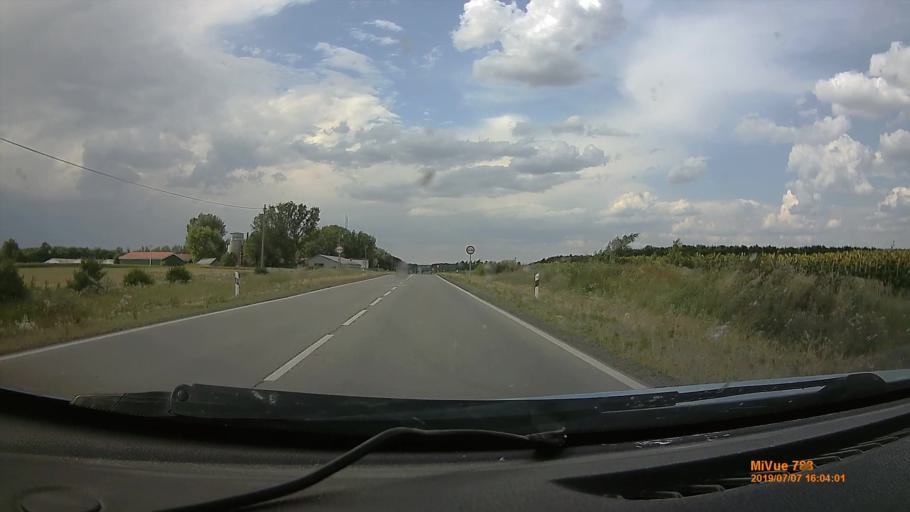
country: HU
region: Heves
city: Hatvan
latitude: 47.6468
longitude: 19.7268
